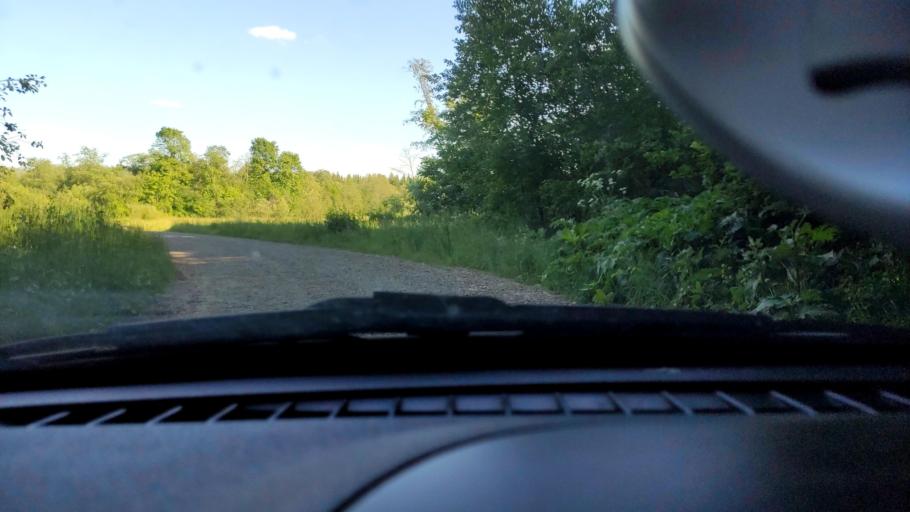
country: RU
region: Perm
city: Bershet'
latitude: 57.6974
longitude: 56.4150
